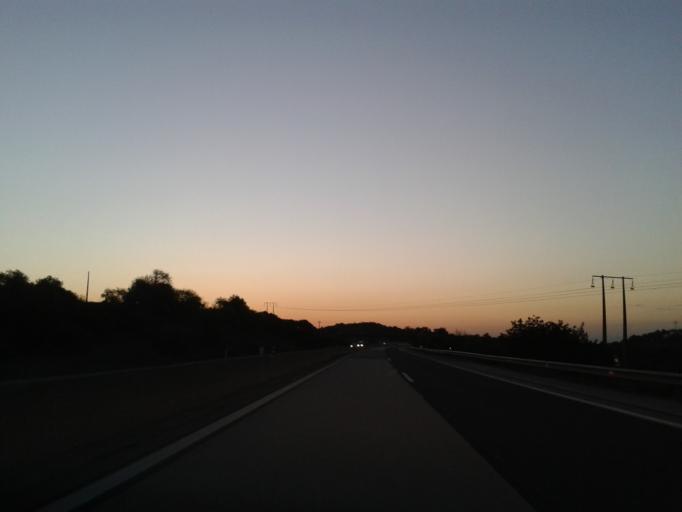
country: PT
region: Faro
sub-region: Loule
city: Boliqueime
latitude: 37.1526
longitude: -8.1732
